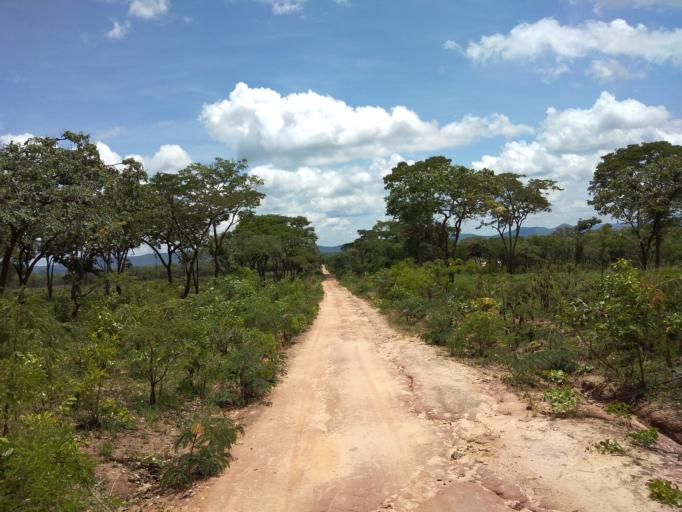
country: ZM
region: Central
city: Mkushi
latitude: -13.9341
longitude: 29.8624
